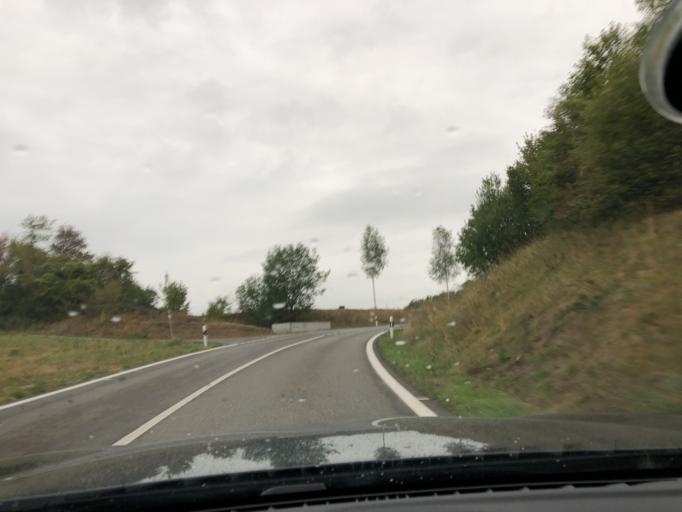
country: CH
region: Aargau
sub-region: Bezirk Bremgarten
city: Berikon
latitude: 47.3473
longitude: 8.3659
